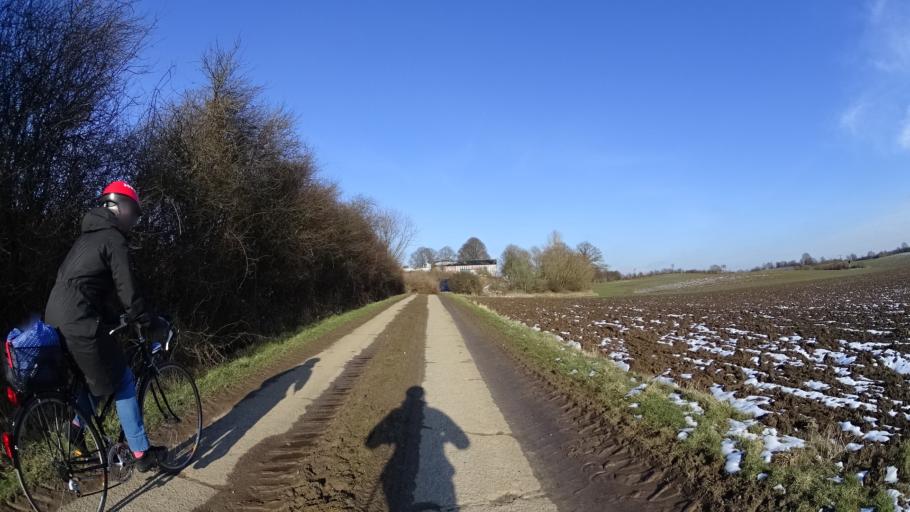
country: DE
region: Schleswig-Holstein
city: Martensrade
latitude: 54.2784
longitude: 10.3795
